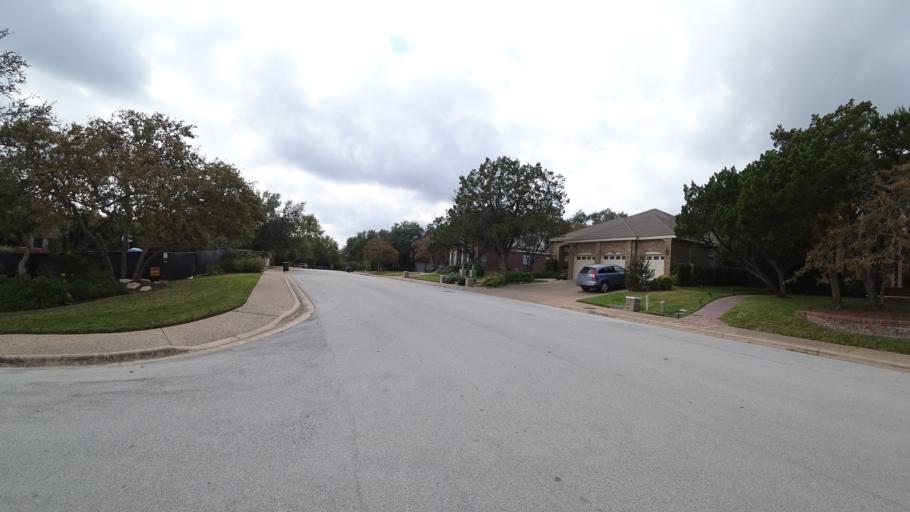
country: US
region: Texas
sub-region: Travis County
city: Barton Creek
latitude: 30.2967
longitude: -97.8957
